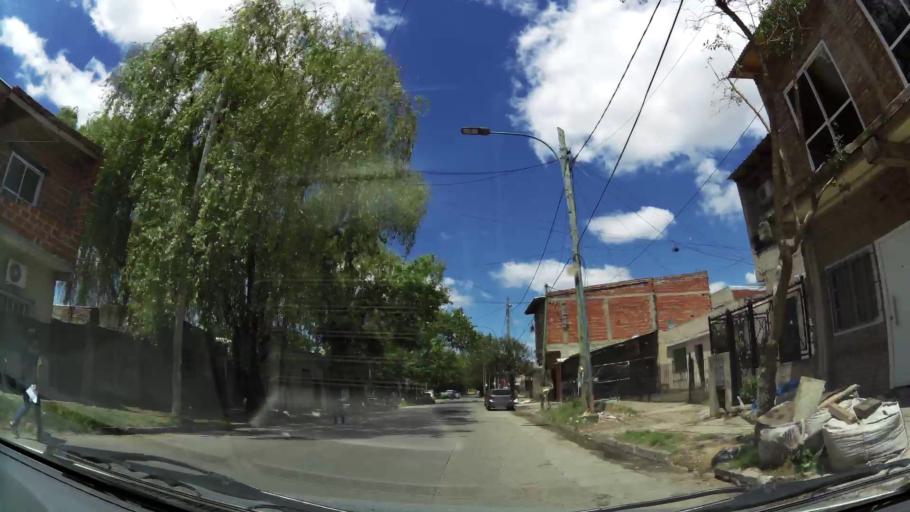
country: AR
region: Buenos Aires
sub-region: Partido de Lanus
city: Lanus
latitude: -34.7197
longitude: -58.4116
